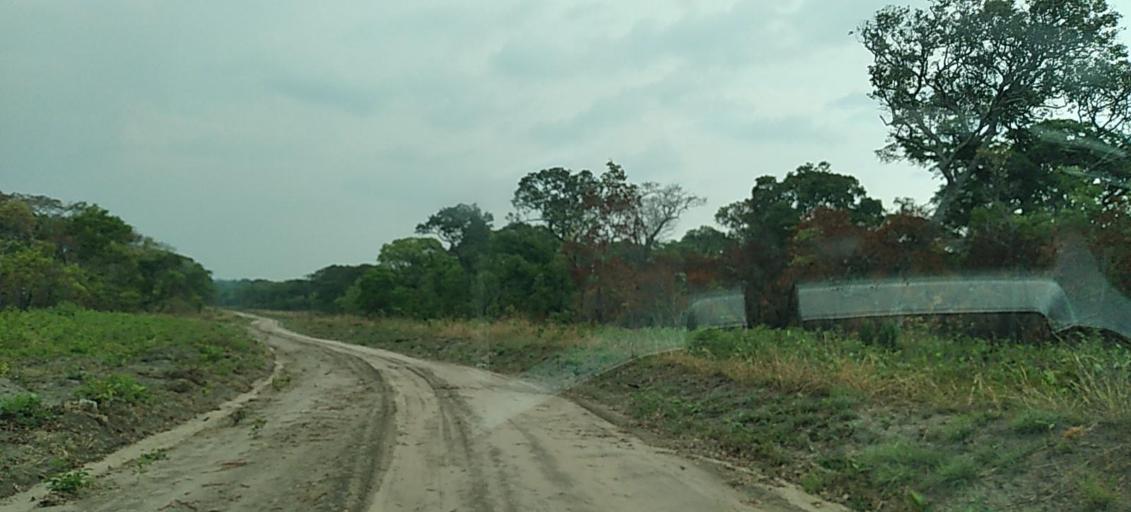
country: ZM
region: North-Western
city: Mwinilunga
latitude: -11.4226
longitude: 24.5945
